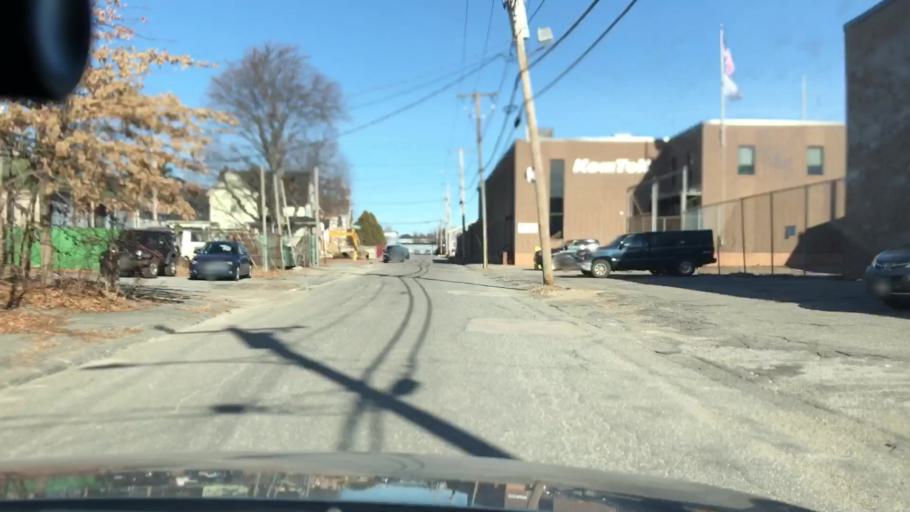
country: US
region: Massachusetts
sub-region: Worcester County
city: Worcester
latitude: 42.3119
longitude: -71.7989
